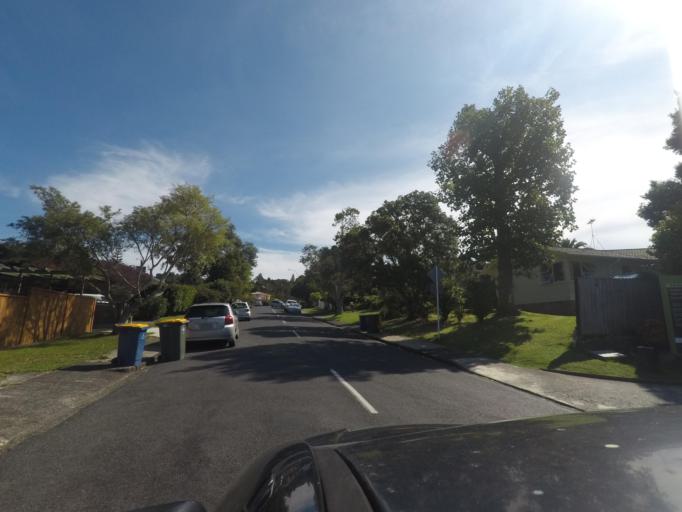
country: NZ
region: Auckland
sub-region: Auckland
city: Titirangi
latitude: -36.9298
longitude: 174.6662
